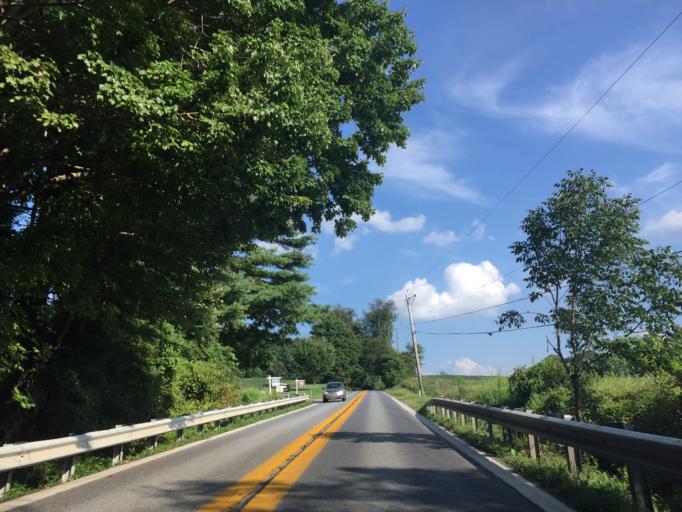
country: US
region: Maryland
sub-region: Carroll County
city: Hampstead
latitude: 39.6099
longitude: -76.7813
